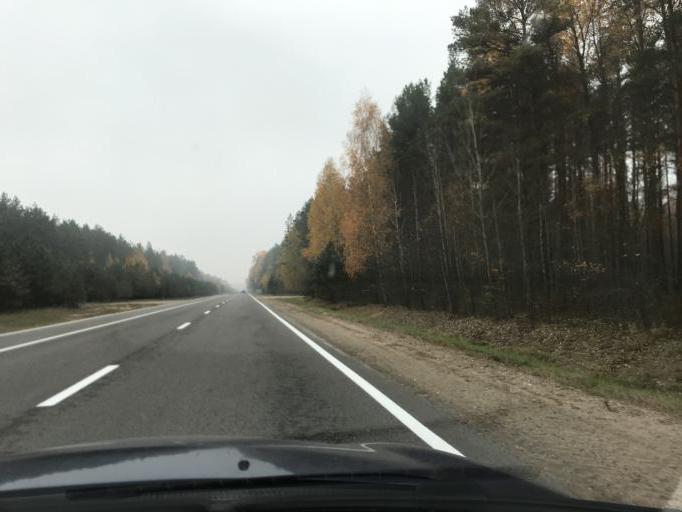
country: LT
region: Alytaus apskritis
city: Druskininkai
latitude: 53.9061
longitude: 23.9186
